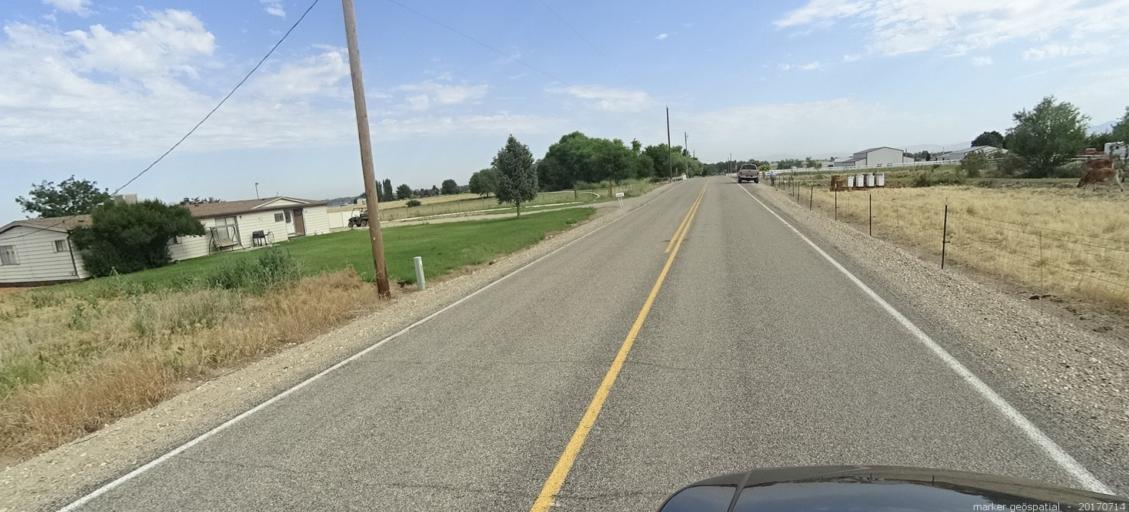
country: US
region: Idaho
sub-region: Ada County
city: Kuna
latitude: 43.4977
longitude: -116.3543
